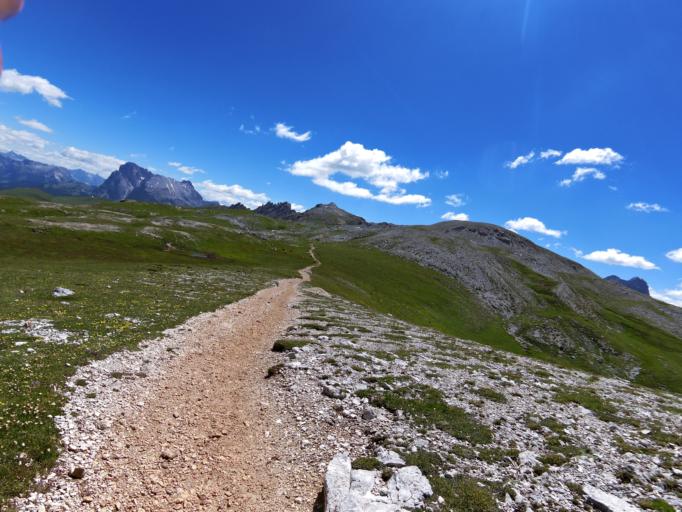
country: IT
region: Trentino-Alto Adige
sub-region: Bolzano
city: Siusi
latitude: 46.5057
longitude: 11.5889
